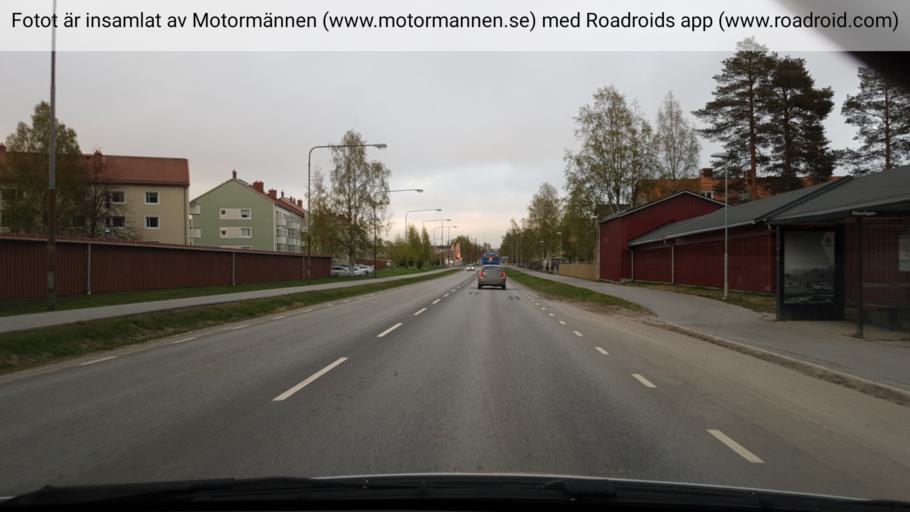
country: SE
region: Vaesterbotten
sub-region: Umea Kommun
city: Umea
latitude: 63.8177
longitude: 20.2368
